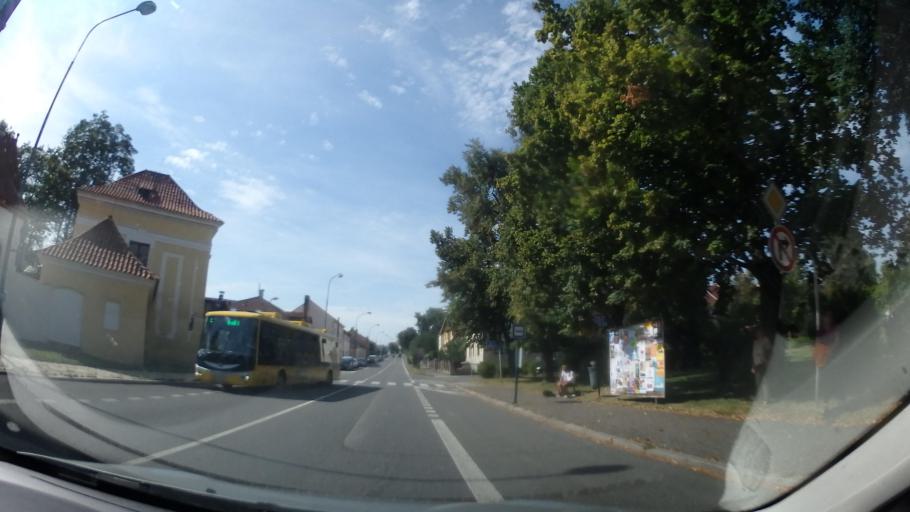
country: CZ
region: Jihocesky
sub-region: Okres Pisek
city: Pisek
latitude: 49.3089
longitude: 14.1326
